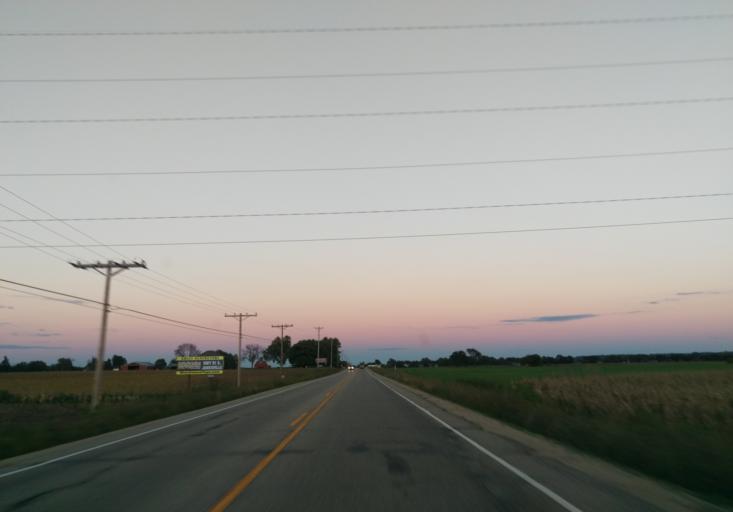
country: US
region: Wisconsin
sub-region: Rock County
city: Janesville
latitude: 42.7304
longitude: -89.1176
